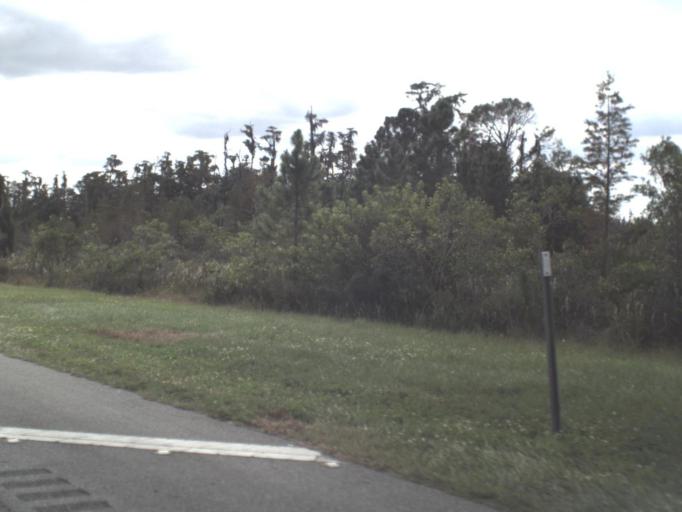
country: US
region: Florida
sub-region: Osceola County
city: Saint Cloud
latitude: 28.1249
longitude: -81.2873
